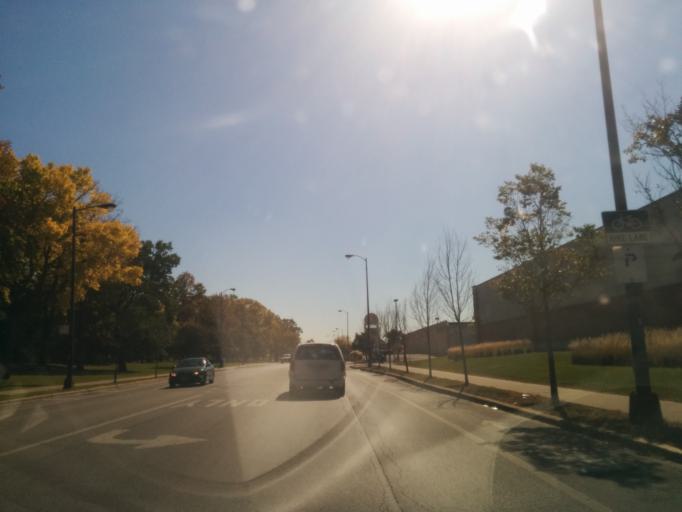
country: US
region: Illinois
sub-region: Cook County
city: Elmwood Park
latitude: 41.9265
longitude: -87.7856
